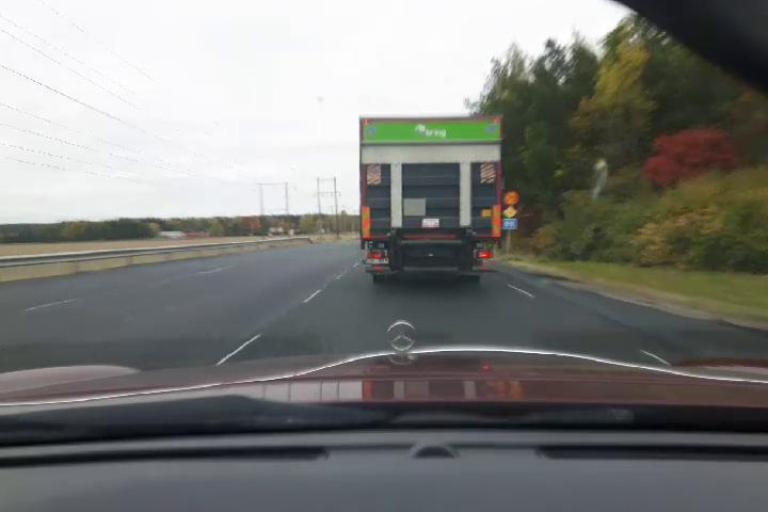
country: SE
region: Uppsala
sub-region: Enkopings Kommun
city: Enkoping
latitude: 59.6331
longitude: 17.0501
